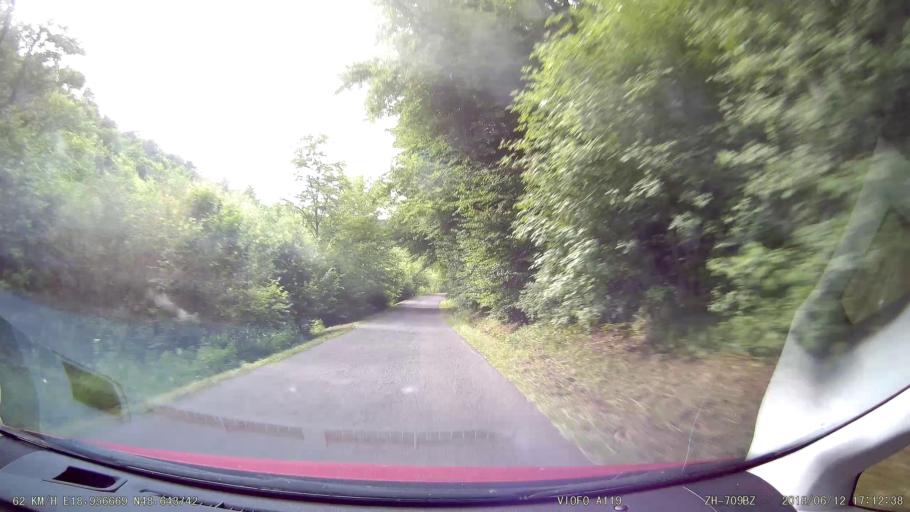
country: SK
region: Banskobystricky
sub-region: Okres Ziar nad Hronom
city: Kremnica
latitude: 48.6439
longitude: 18.9565
